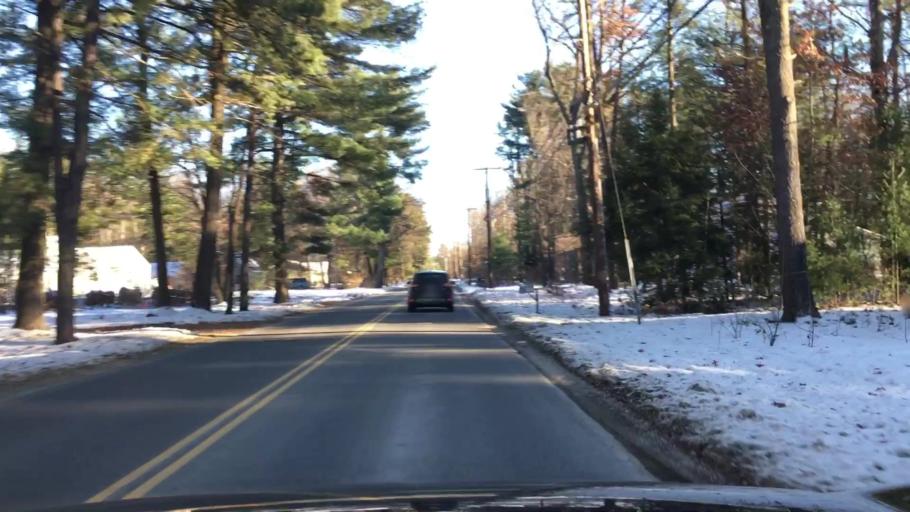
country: US
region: New Hampshire
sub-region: Hillsborough County
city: Milford
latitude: 42.8179
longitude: -71.5769
